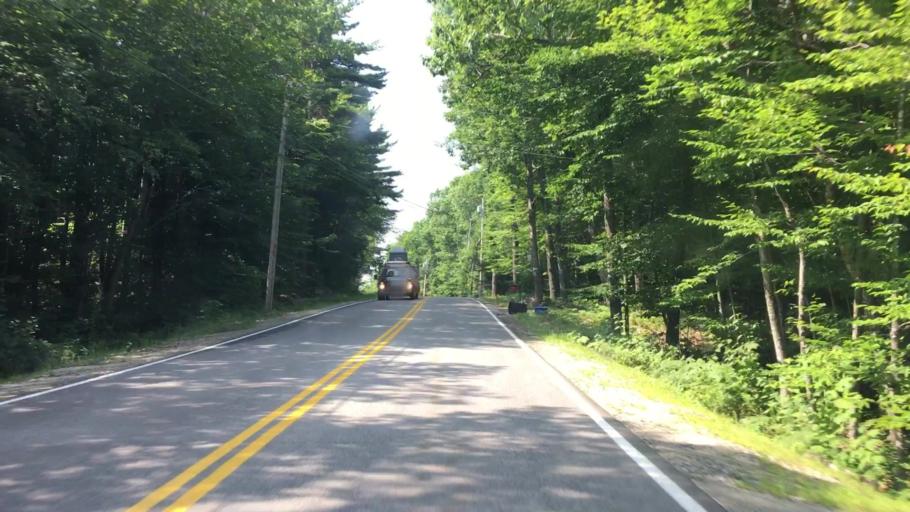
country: US
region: Maine
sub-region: Cumberland County
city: Raymond
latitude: 43.9652
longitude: -70.4136
